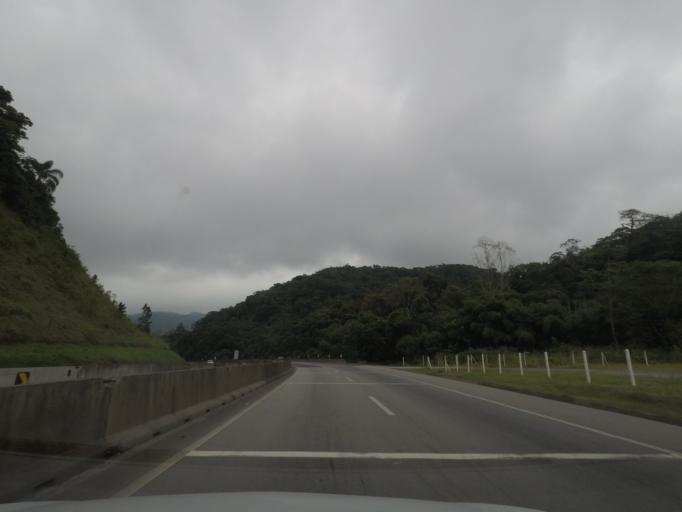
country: BR
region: Sao Paulo
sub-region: Juquitiba
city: Juquitiba
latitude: -24.0462
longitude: -47.1964
